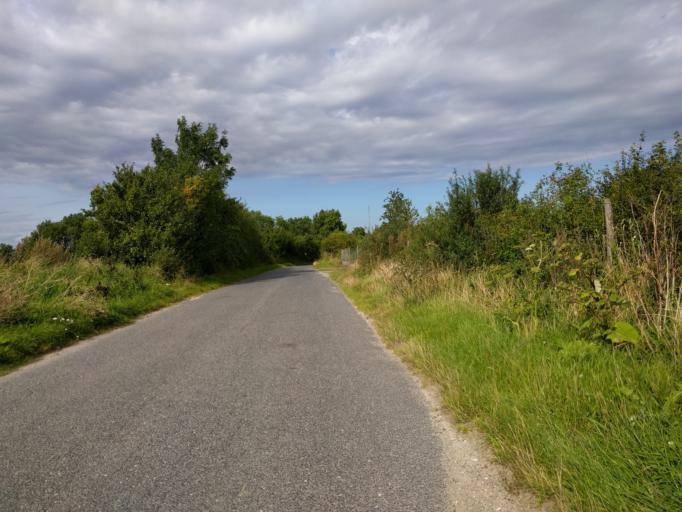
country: DK
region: South Denmark
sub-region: Kerteminde Kommune
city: Kerteminde
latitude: 55.4627
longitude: 10.6235
